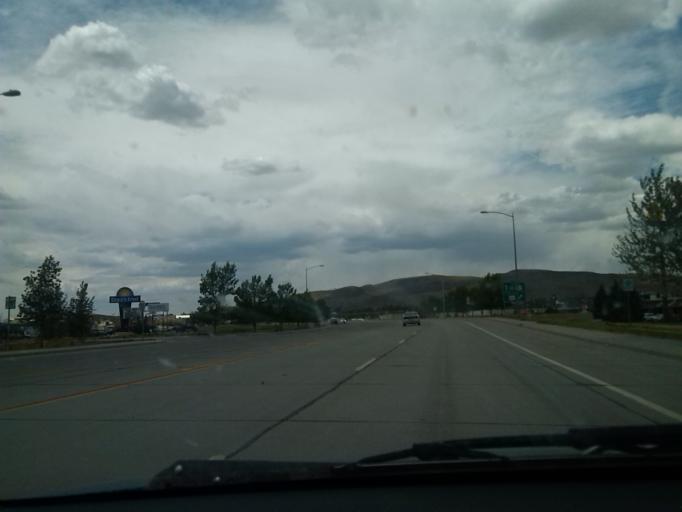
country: US
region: Wyoming
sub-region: Carbon County
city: Rawlins
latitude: 41.7925
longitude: -107.2104
